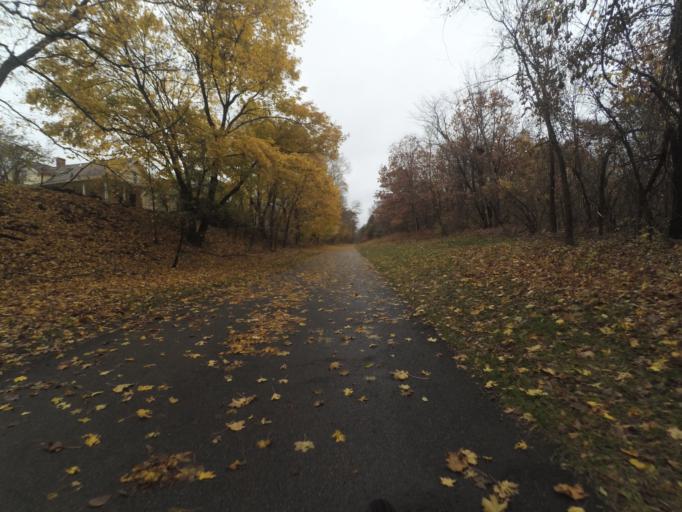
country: US
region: Massachusetts
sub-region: Middlesex County
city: Lexington
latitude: 42.4335
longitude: -71.2071
